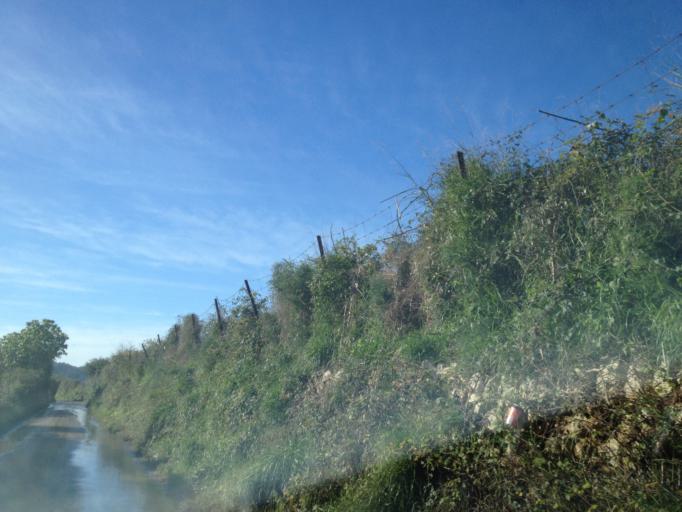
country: ES
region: Balearic Islands
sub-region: Illes Balears
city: Sineu
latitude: 39.6447
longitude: 3.0332
